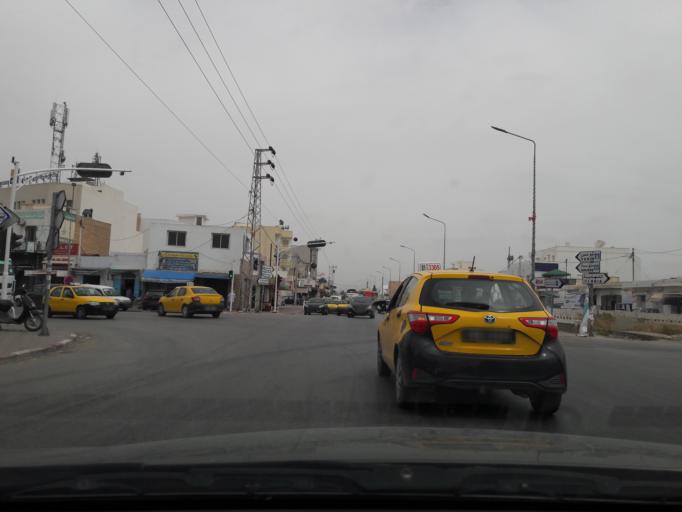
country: TN
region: Safaqis
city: Al Qarmadah
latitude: 34.8022
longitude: 10.7613
